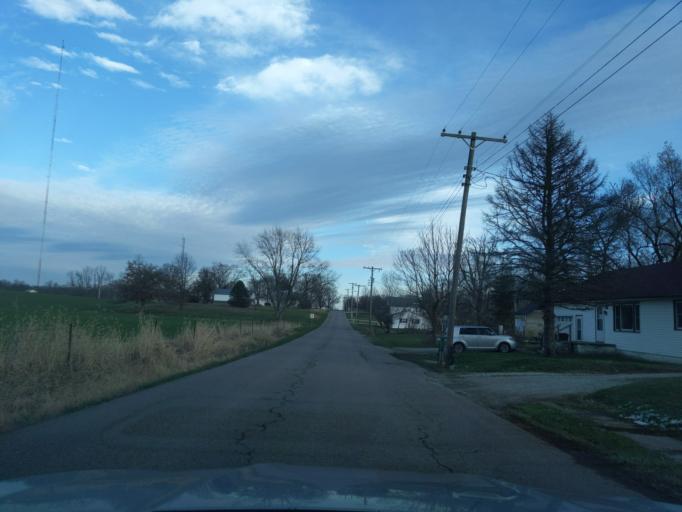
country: US
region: Indiana
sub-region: Decatur County
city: Westport
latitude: 39.2347
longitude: -85.5708
